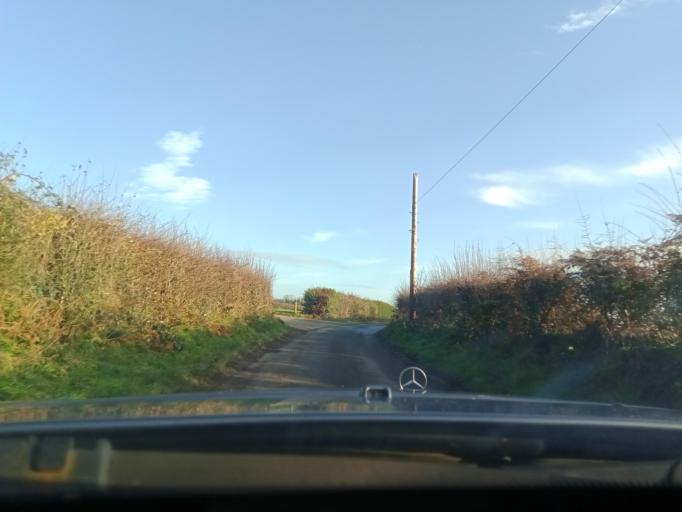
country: IE
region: Munster
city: Carrick-on-Suir
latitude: 52.4382
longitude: -7.4064
